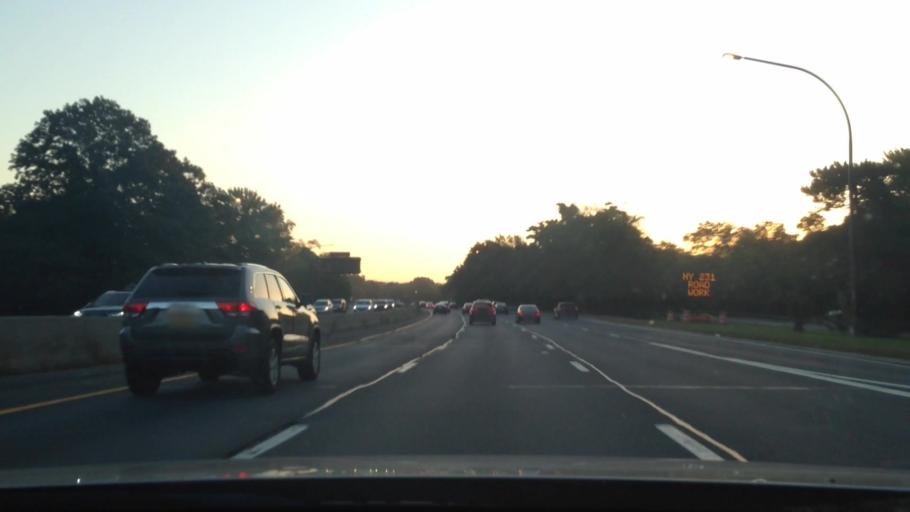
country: US
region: New York
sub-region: Suffolk County
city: West Babylon
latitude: 40.7321
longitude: -73.3439
